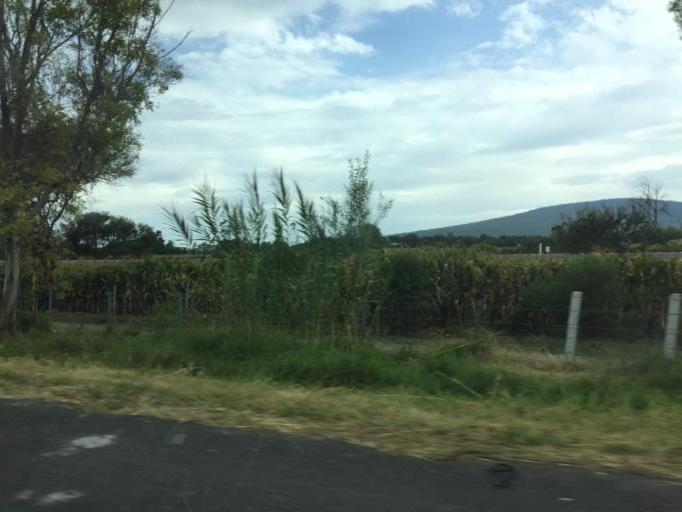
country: MX
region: Jalisco
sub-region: Ocotlan
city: Joconoxtle (La Tuna)
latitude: 20.3785
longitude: -102.6850
